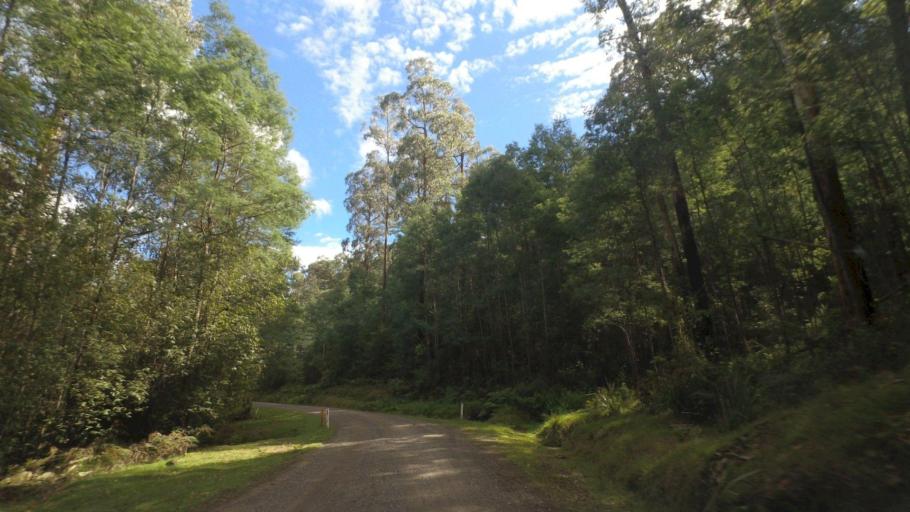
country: AU
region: Victoria
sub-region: Cardinia
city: Bunyip
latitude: -37.9811
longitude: 145.8154
